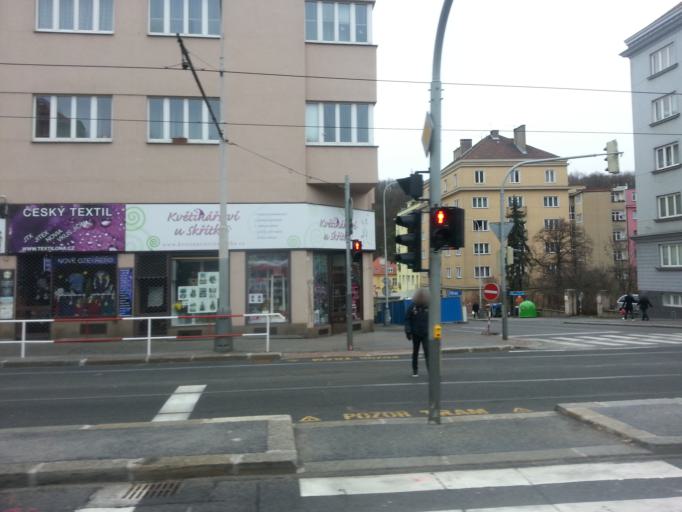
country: CZ
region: Praha
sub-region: Praha 1
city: Mala Strana
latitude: 50.0708
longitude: 14.3803
